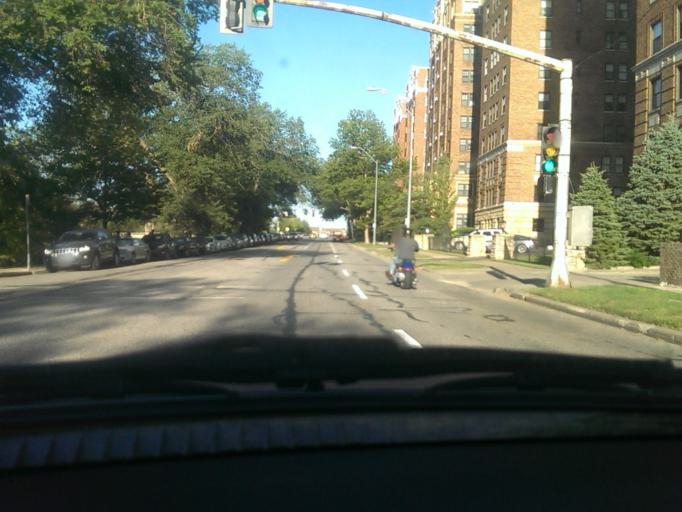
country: US
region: Kansas
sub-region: Johnson County
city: Westwood
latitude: 39.0400
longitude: -94.5904
